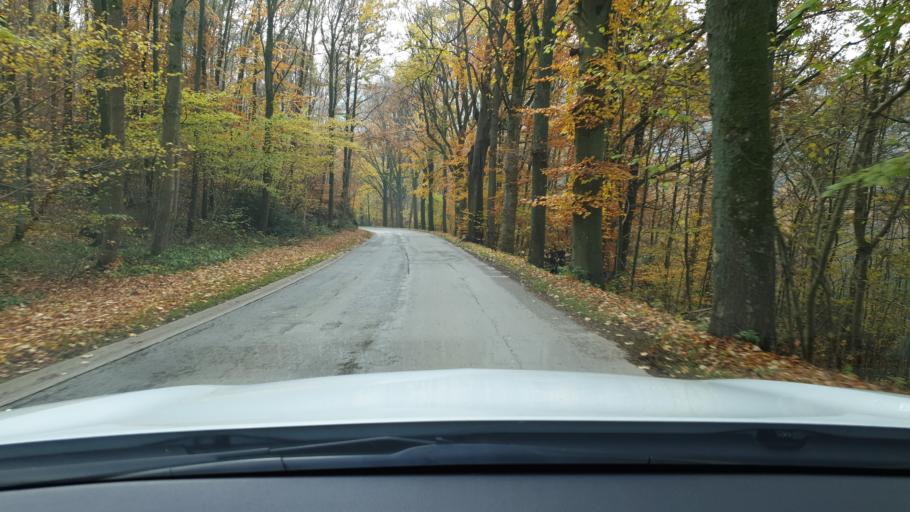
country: BE
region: Wallonia
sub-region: Province de Liege
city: Trois-Ponts
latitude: 50.4055
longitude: 5.8652
